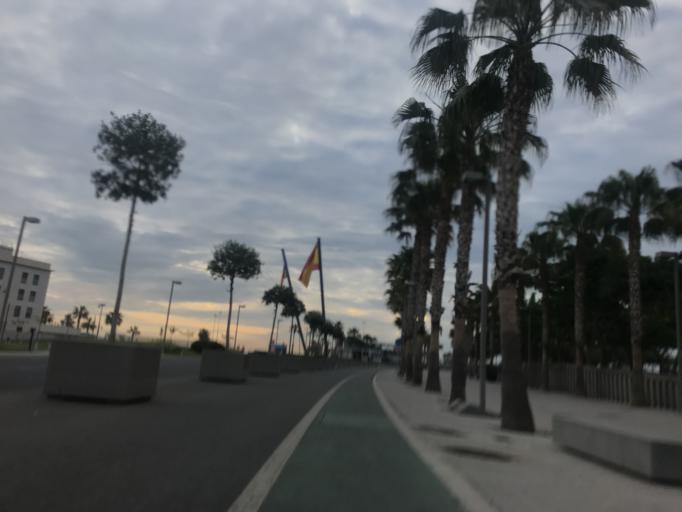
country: ES
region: Valencia
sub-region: Provincia de Valencia
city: Alboraya
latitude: 39.4621
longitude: -0.3241
